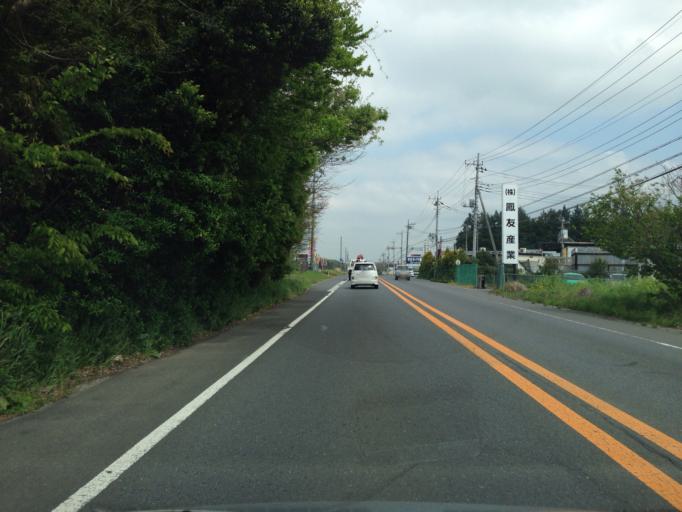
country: JP
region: Ibaraki
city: Iwase
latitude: 36.3515
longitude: 140.0649
